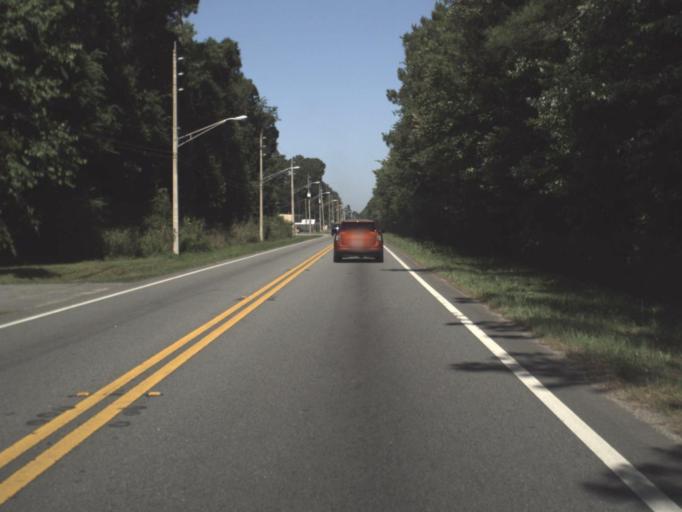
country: US
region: Florida
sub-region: Duval County
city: Jacksonville
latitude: 30.3233
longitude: -81.7615
